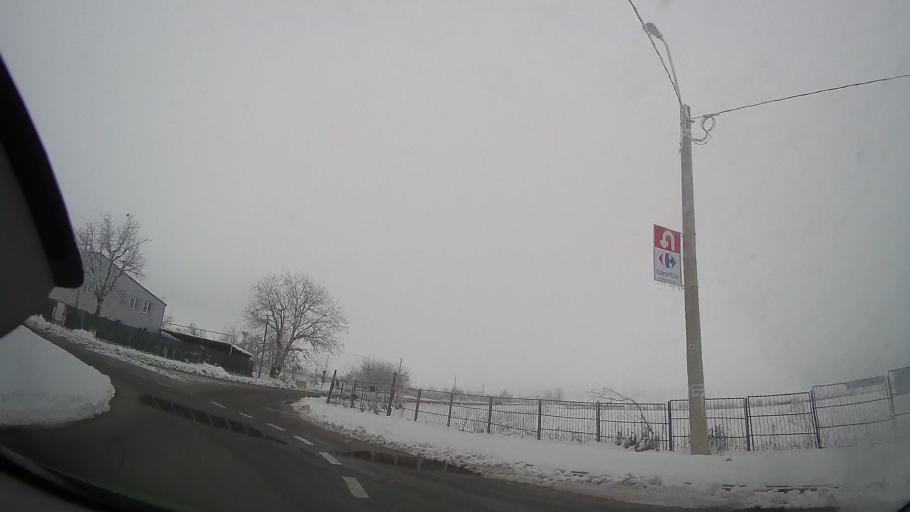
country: RO
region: Neamt
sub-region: Comuna Horia
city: Cotu Vames
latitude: 46.9384
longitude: 26.9489
